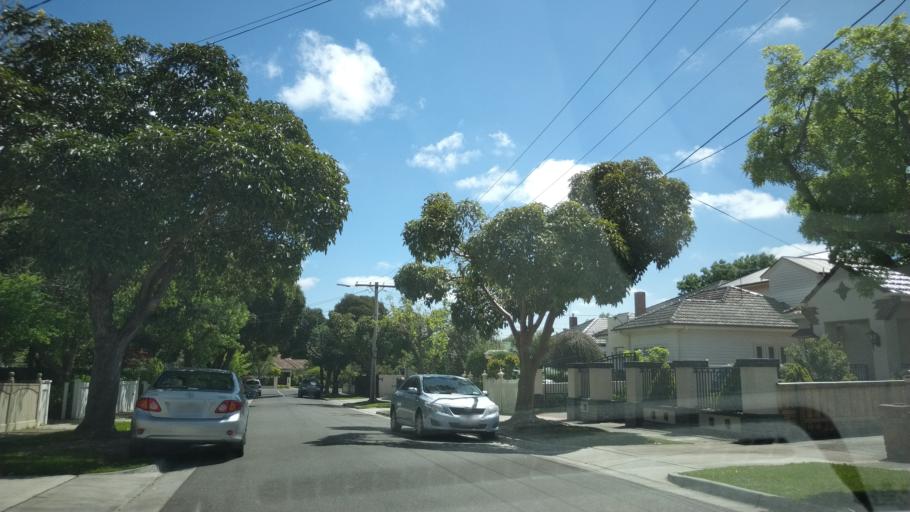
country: AU
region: Victoria
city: Hughesdale
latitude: -37.9009
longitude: 145.0768
